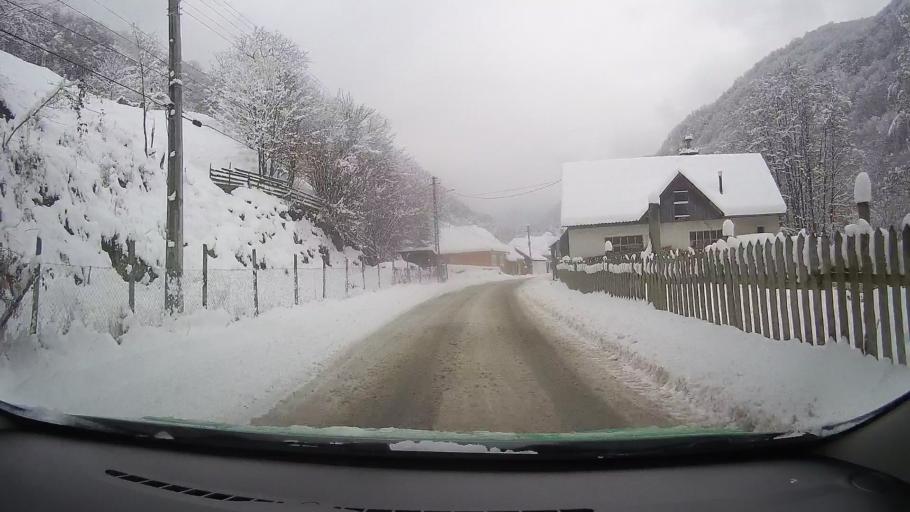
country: RO
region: Alba
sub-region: Comuna Sugag
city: Dobra
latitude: 45.7611
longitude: 23.6600
